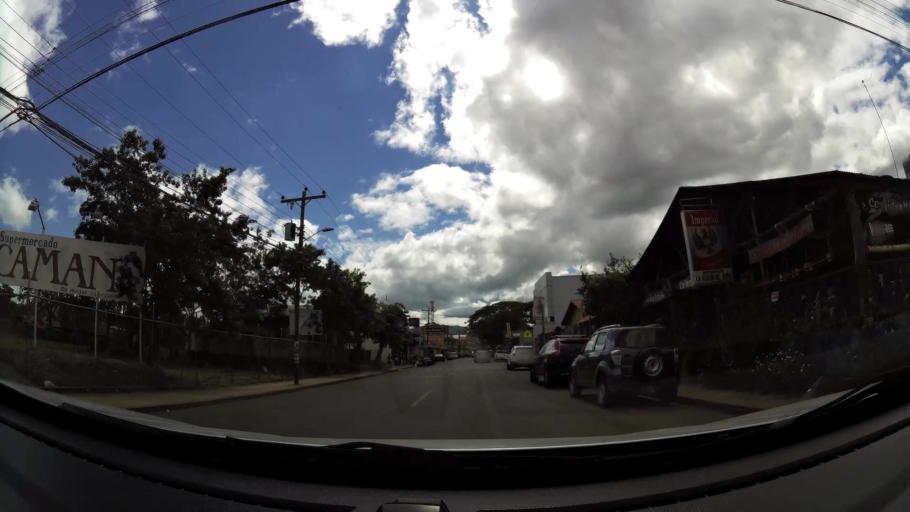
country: CR
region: Guanacaste
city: Santa Cruz
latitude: 10.2649
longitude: -85.5866
